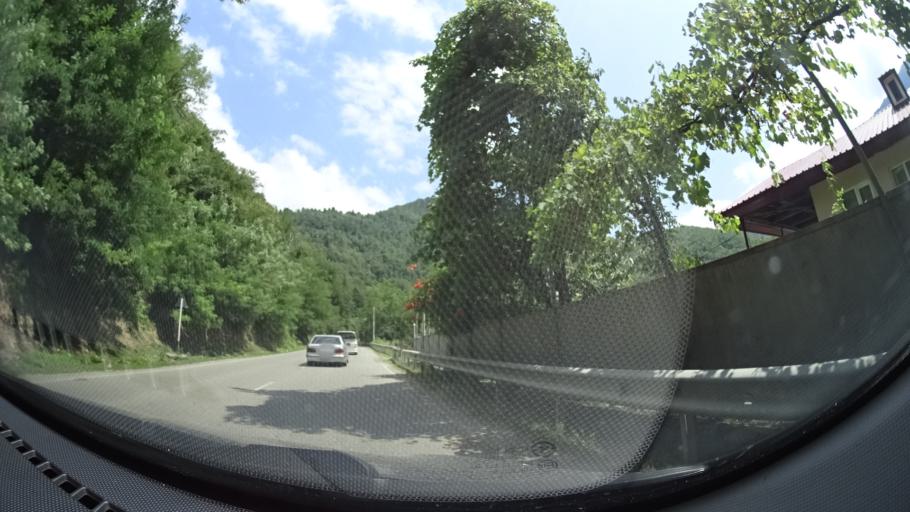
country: GE
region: Ajaria
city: Keda
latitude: 41.5709
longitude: 41.8552
